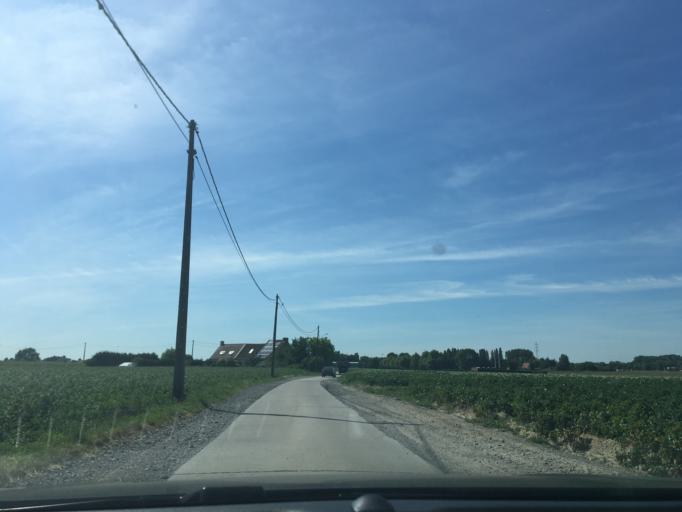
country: BE
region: Flanders
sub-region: Provincie West-Vlaanderen
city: Tielt
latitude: 50.9756
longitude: 3.3202
